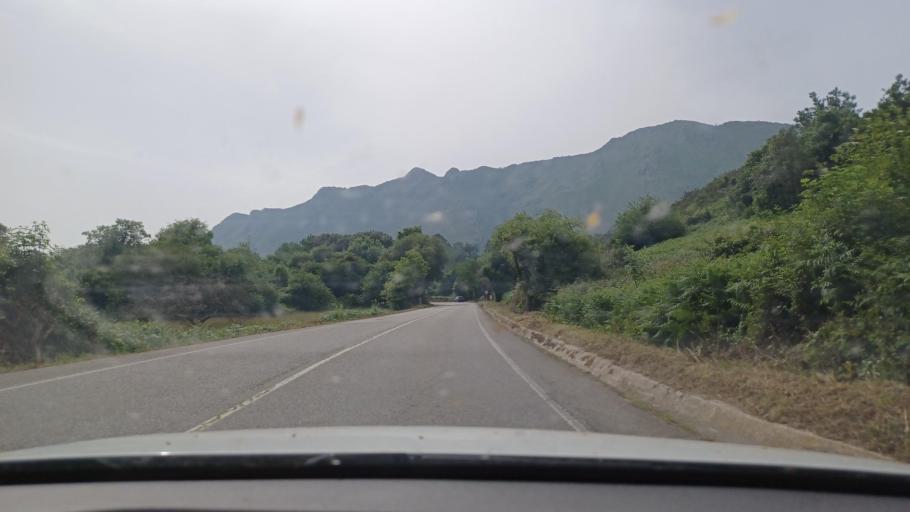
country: ES
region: Asturias
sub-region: Province of Asturias
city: Ribadesella
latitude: 43.4427
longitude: -4.9974
